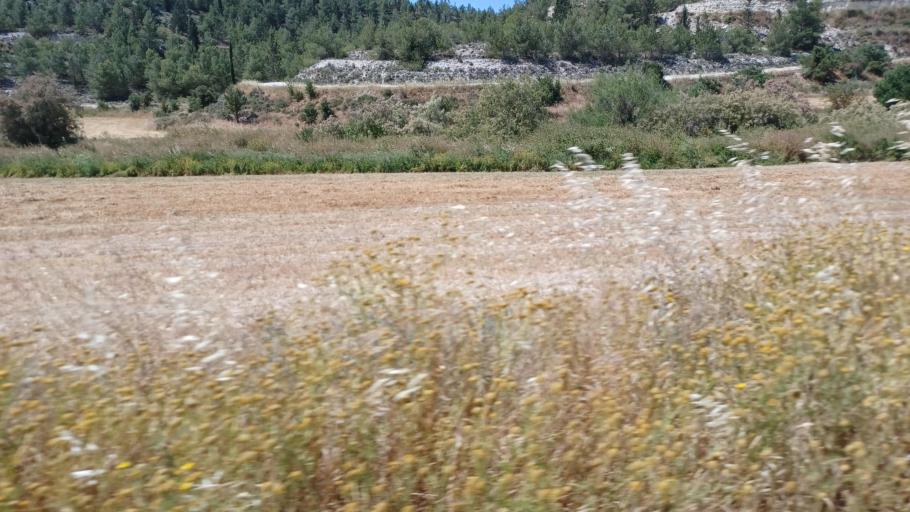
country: CY
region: Lefkosia
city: Lympia
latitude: 34.9950
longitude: 33.5235
